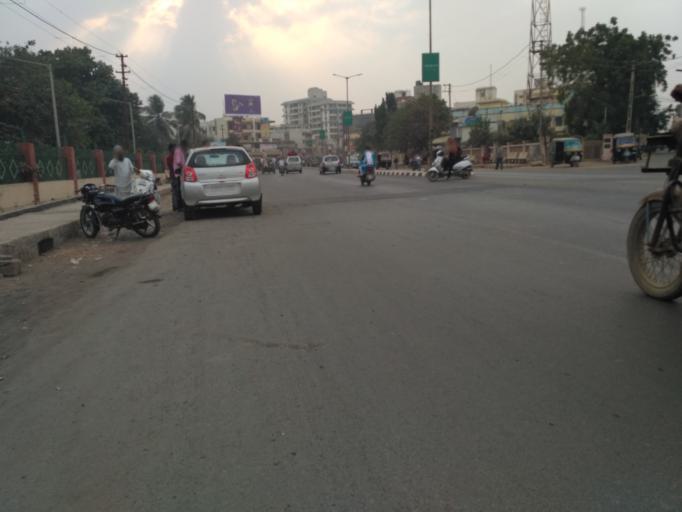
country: IN
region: Gujarat
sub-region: Porbandar
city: Porbandar
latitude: 21.6392
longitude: 69.6241
